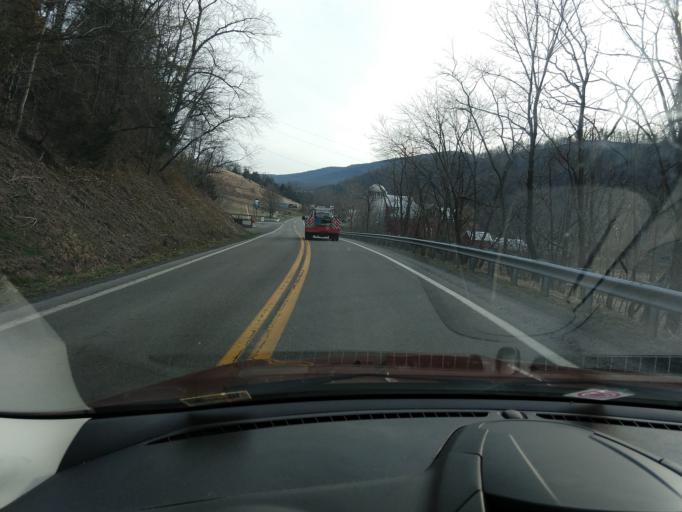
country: US
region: West Virginia
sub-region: Pendleton County
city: Franklin
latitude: 38.6167
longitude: -79.3488
